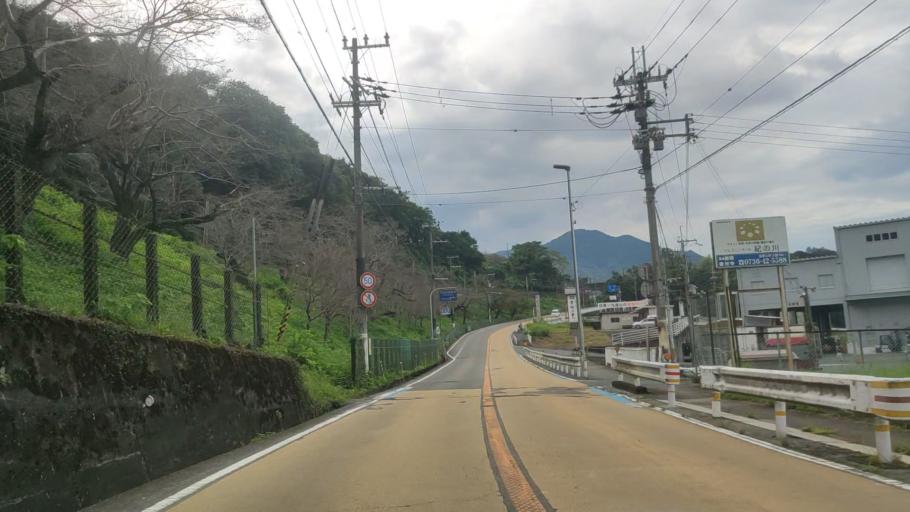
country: JP
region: Wakayama
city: Hashimoto
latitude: 34.2893
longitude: 135.5697
